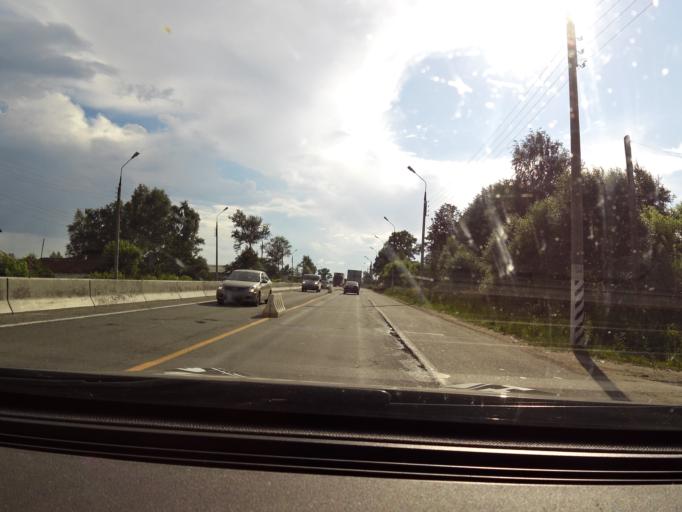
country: RU
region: Nizjnij Novgorod
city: Mulino
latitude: 56.2716
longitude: 42.9551
